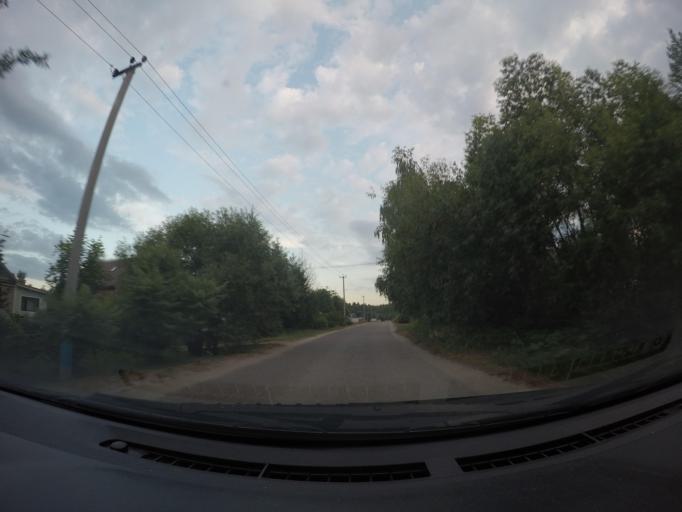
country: RU
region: Moskovskaya
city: Krasnyy Tkach
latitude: 55.3830
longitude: 39.2044
